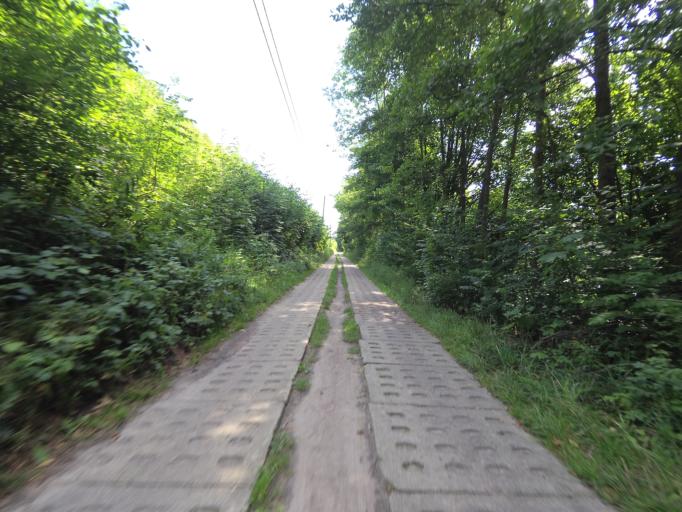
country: PL
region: Pomeranian Voivodeship
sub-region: Gdynia
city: Wielki Kack
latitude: 54.4879
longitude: 18.5050
